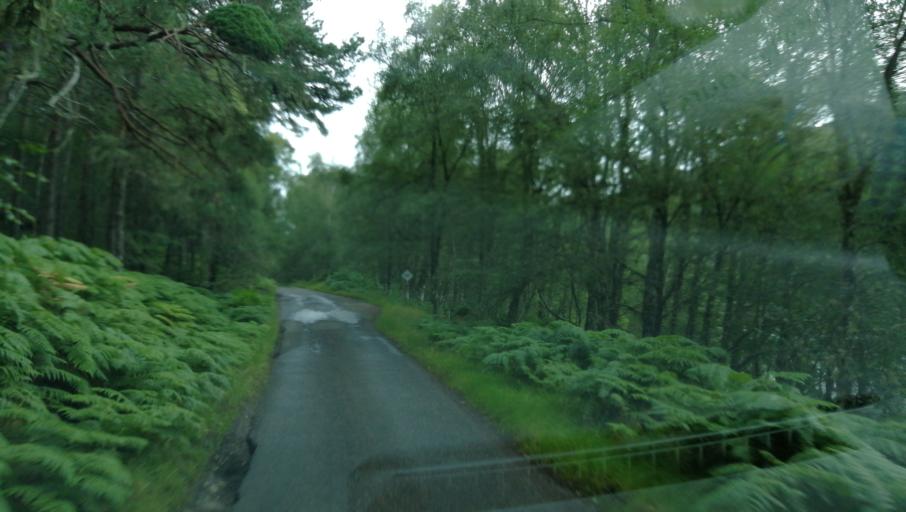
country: GB
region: Scotland
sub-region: Highland
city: Spean Bridge
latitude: 57.3056
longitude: -4.8730
